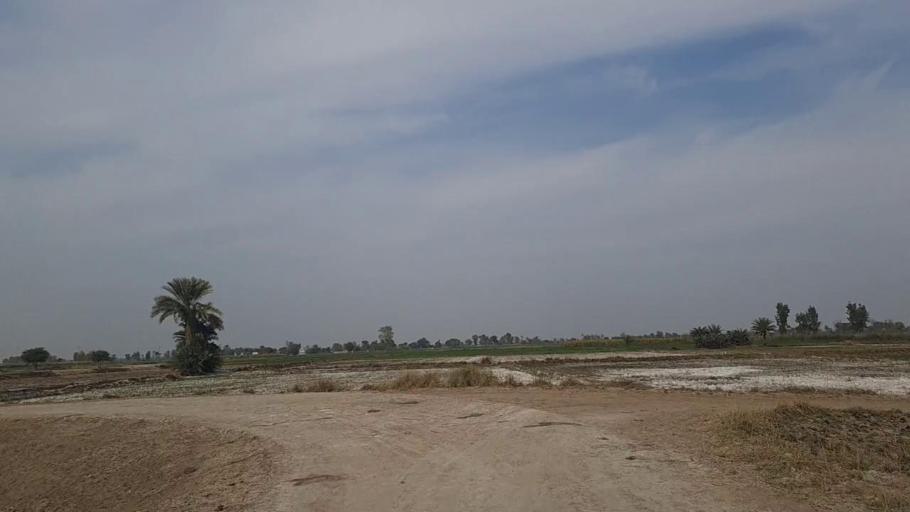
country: PK
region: Sindh
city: Daur
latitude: 26.4828
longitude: 68.4054
